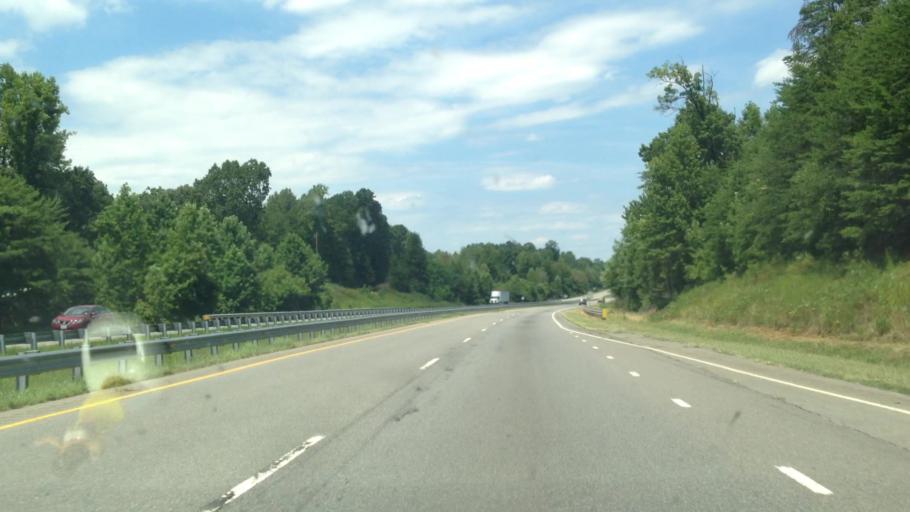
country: US
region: North Carolina
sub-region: Rockingham County
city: Stoneville
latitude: 36.5058
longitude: -79.9207
